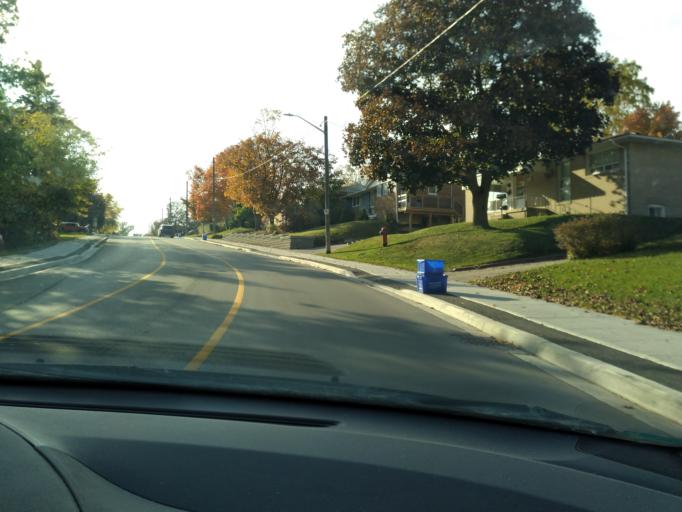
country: CA
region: Ontario
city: Newmarket
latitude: 44.0548
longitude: -79.4694
